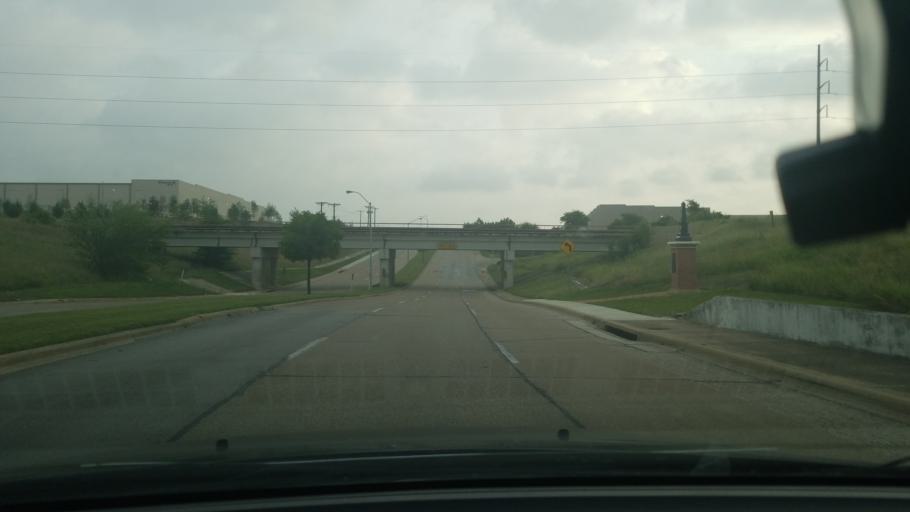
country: US
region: Texas
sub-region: Dallas County
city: Mesquite
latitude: 32.7729
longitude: -96.6290
